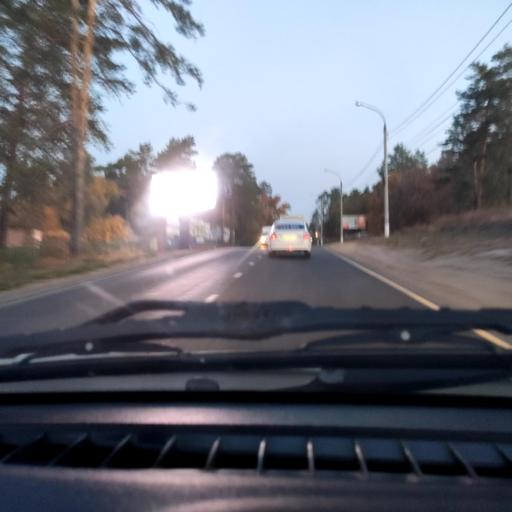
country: RU
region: Samara
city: Tol'yatti
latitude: 53.4839
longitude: 49.3170
